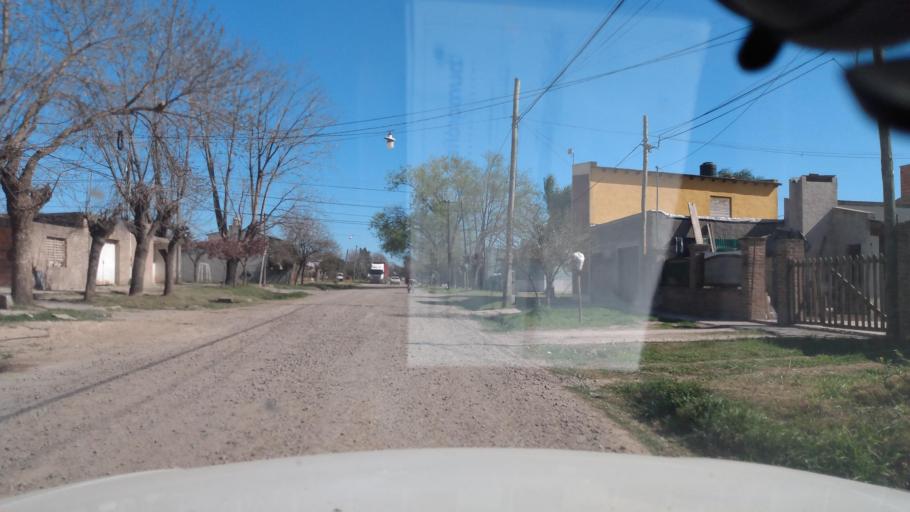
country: AR
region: Buenos Aires
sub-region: Partido de Mercedes
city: Mercedes
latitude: -34.6558
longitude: -59.4146
